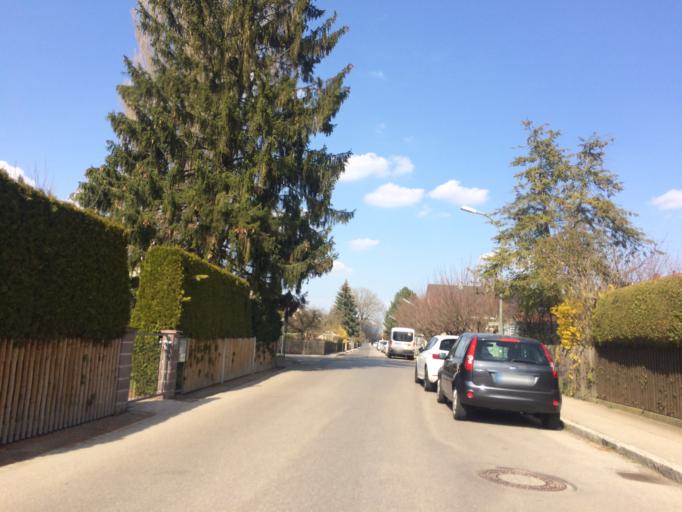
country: DE
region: Bavaria
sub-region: Swabia
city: Gersthofen
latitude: 48.4073
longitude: 10.8965
